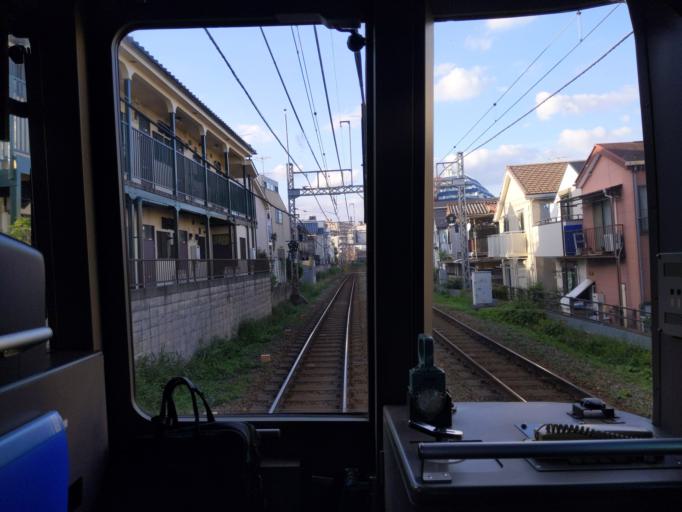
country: JP
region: Tokyo
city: Tokyo
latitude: 35.6651
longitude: 139.6521
